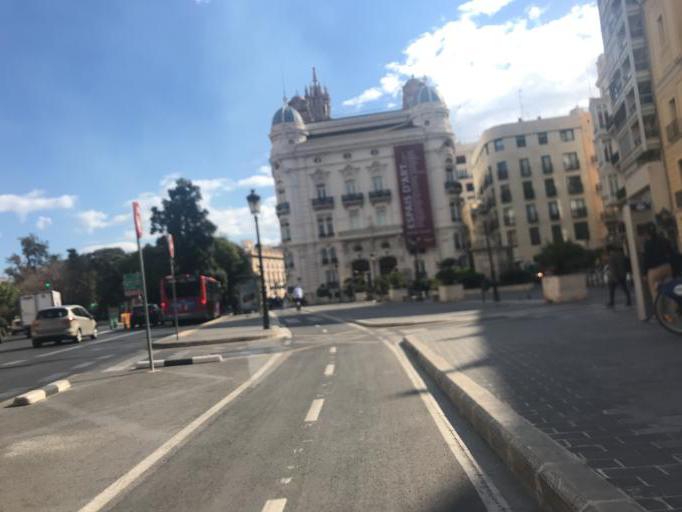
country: ES
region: Valencia
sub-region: Provincia de Valencia
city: Valencia
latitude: 39.4746
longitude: -0.3699
